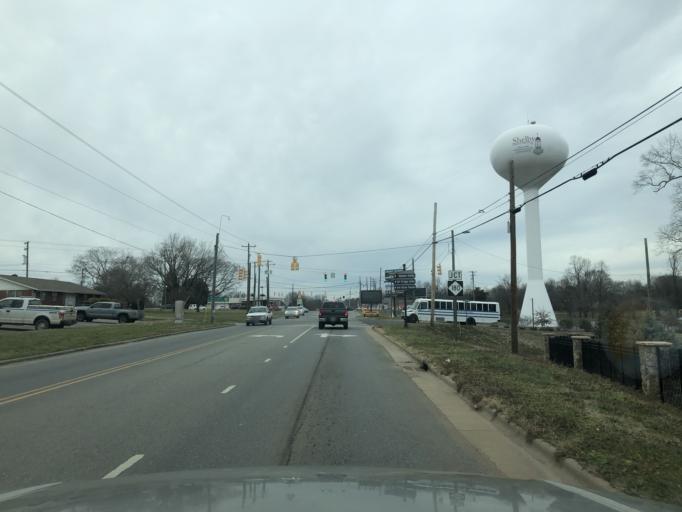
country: US
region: North Carolina
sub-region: Cleveland County
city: Shelby
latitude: 35.2821
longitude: -81.4907
